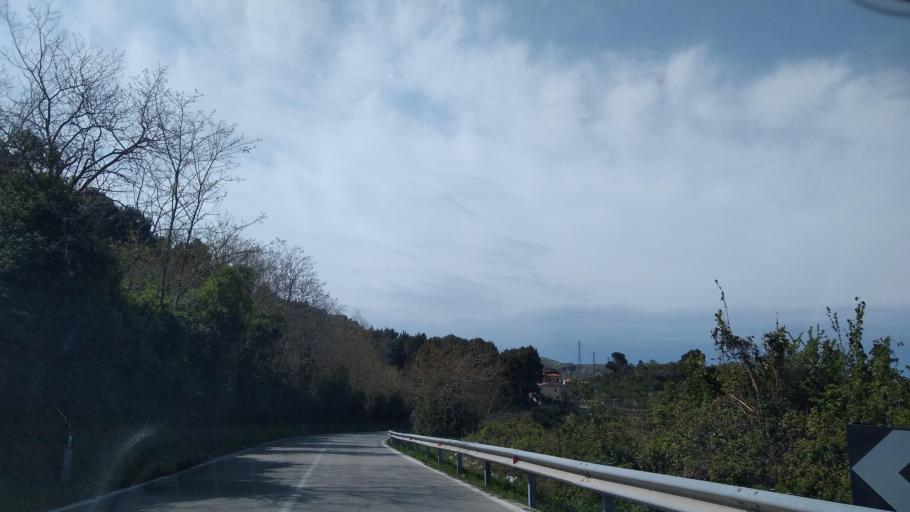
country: IT
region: Sicily
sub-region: Palermo
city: Pioppo
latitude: 38.0392
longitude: 13.2043
